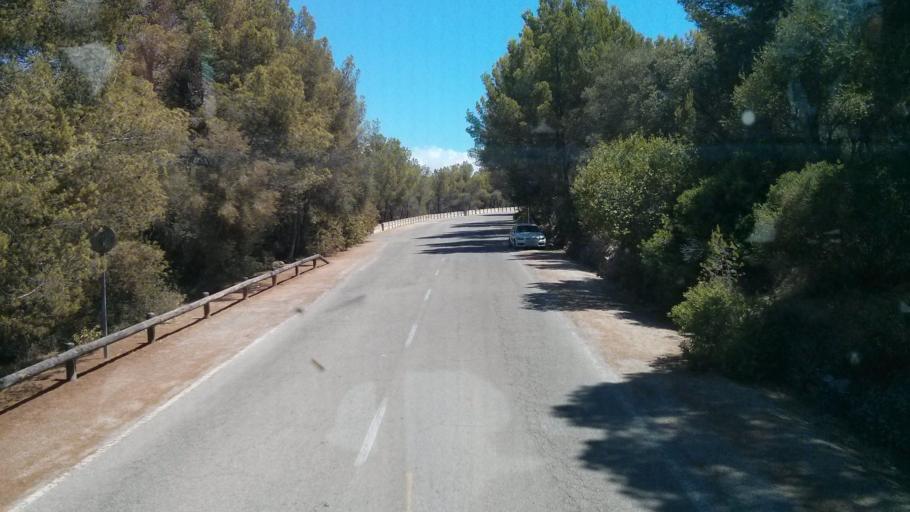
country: ES
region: Balearic Islands
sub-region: Illes Balears
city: Palma
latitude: 39.5651
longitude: 2.6176
